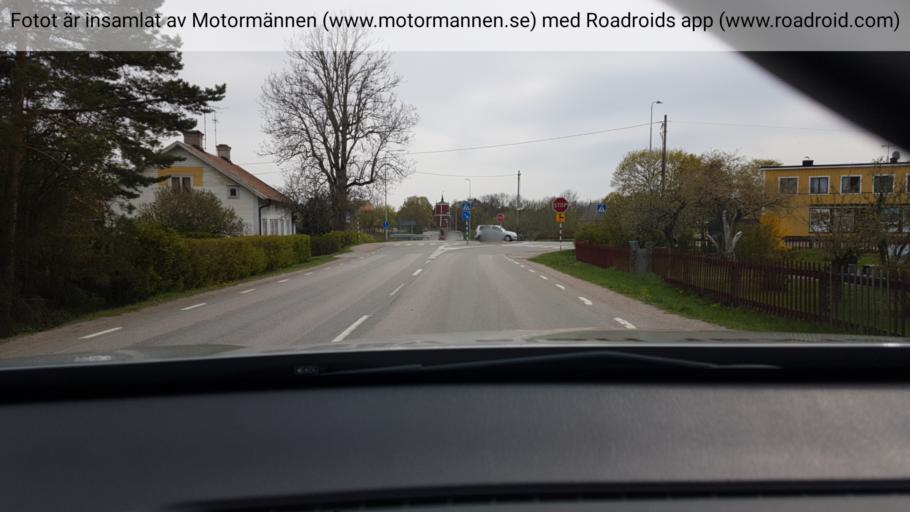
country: SE
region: Stockholm
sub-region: Norrtalje Kommun
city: Nykvarn
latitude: 59.8689
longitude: 18.0713
